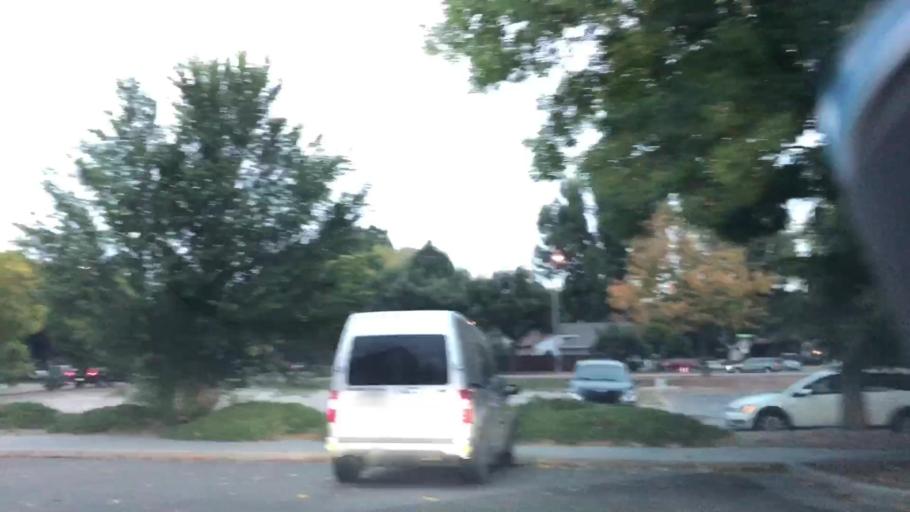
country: US
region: Colorado
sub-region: Larimer County
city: Fort Collins
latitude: 40.5663
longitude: -105.0559
